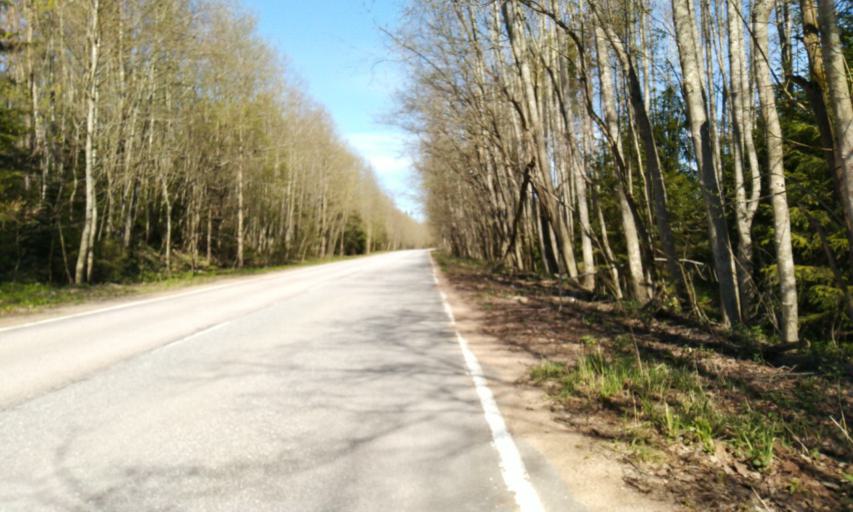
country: RU
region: Leningrad
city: Garbolovo
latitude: 60.4066
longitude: 30.4659
